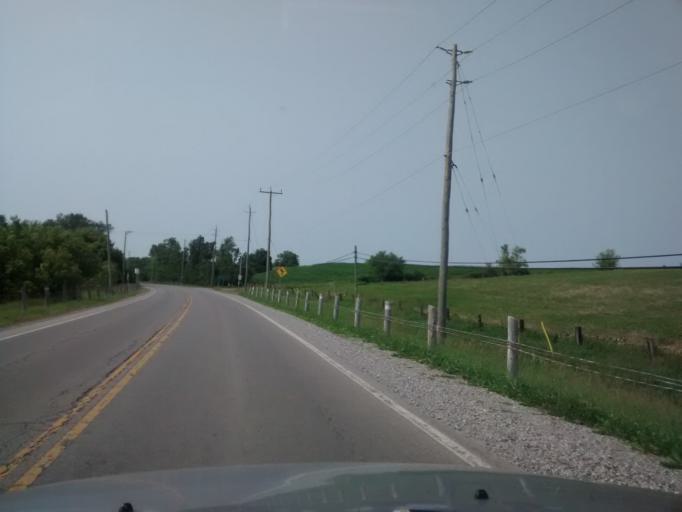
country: CA
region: Ontario
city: Ancaster
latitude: 43.0279
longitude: -79.8913
